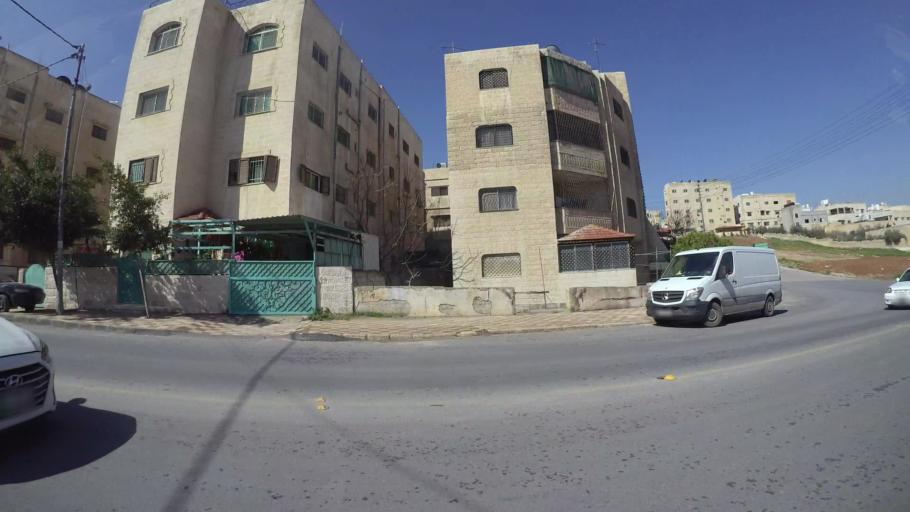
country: JO
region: Amman
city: Amman
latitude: 31.9869
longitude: 35.9835
